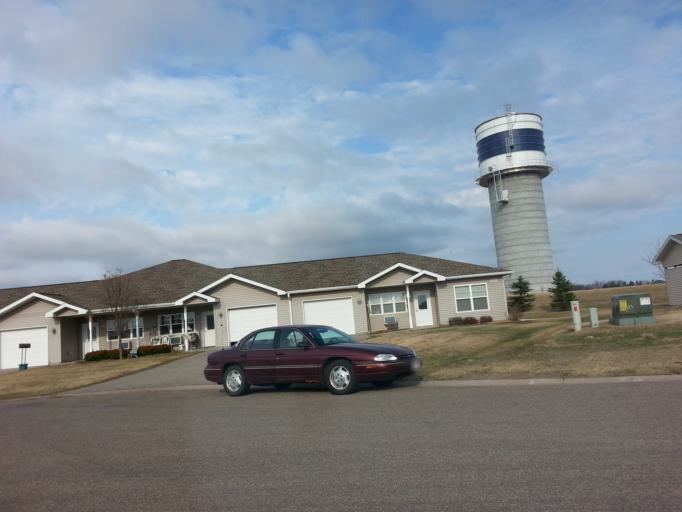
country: US
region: Wisconsin
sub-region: Pierce County
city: Ellsworth
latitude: 44.7508
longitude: -92.4937
